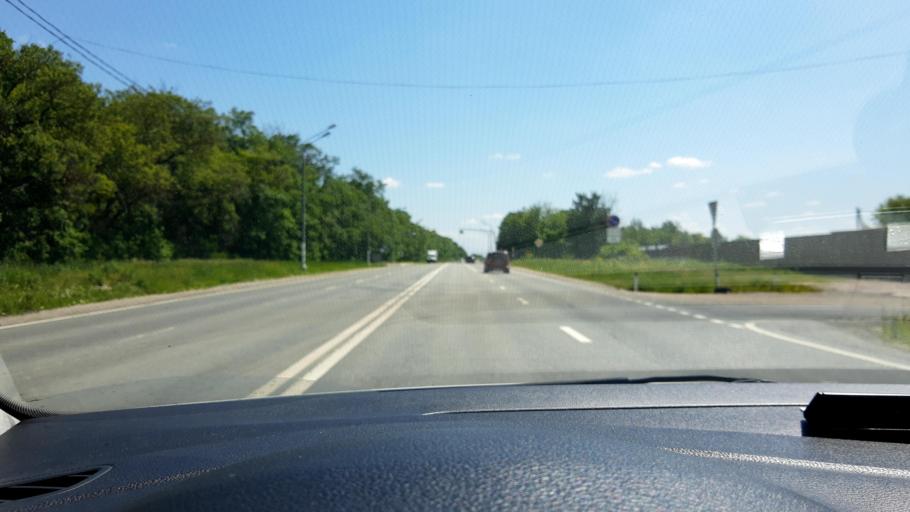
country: RU
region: Moskovskaya
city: Bronnitsy
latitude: 55.4787
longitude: 38.1807
